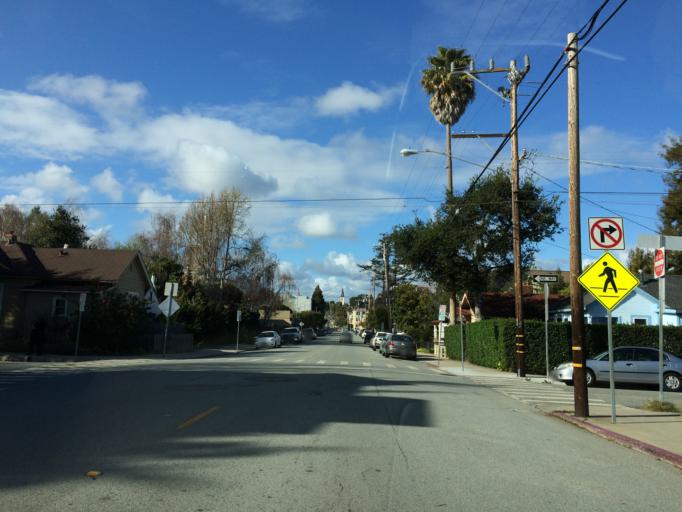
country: US
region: California
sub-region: Santa Cruz County
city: Santa Cruz
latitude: 36.9705
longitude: -122.0276
